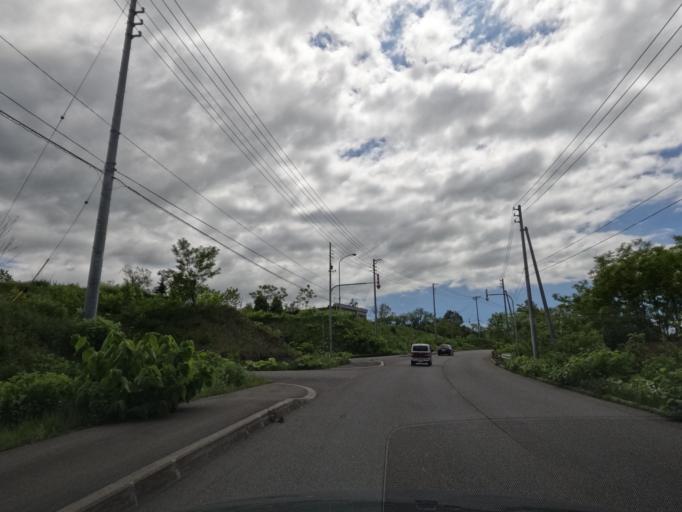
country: JP
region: Hokkaido
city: Bibai
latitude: 43.2551
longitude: 141.9303
